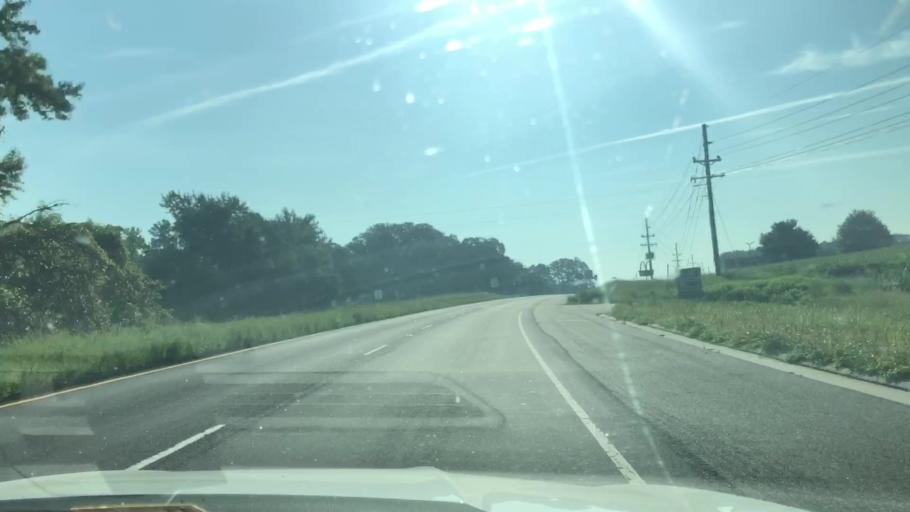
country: US
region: Virginia
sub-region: Richmond County
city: Warsaw
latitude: 37.9654
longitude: -76.7885
